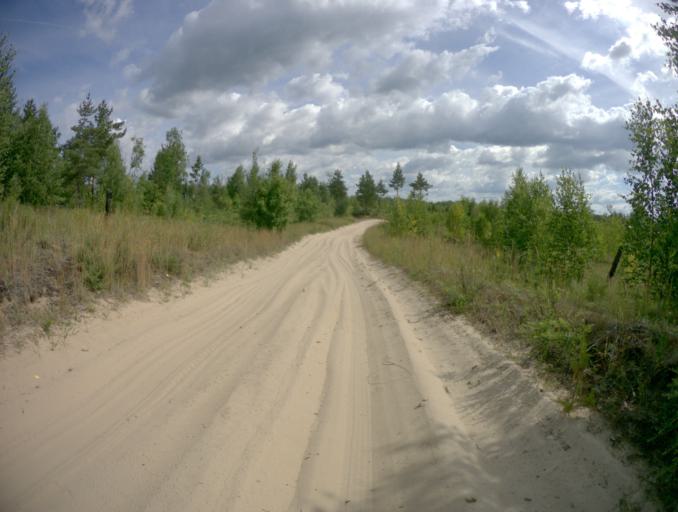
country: RU
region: Ivanovo
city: Talitsy
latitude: 56.5364
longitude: 42.4466
